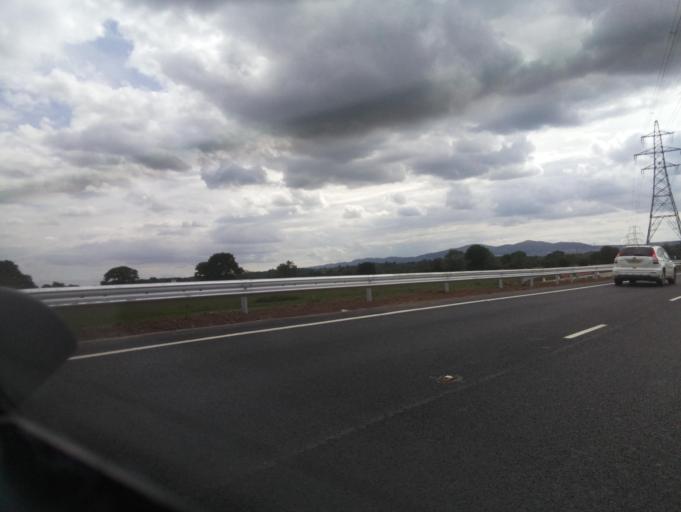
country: GB
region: England
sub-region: Worcestershire
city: Kempsey
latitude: 52.1622
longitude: -2.2206
